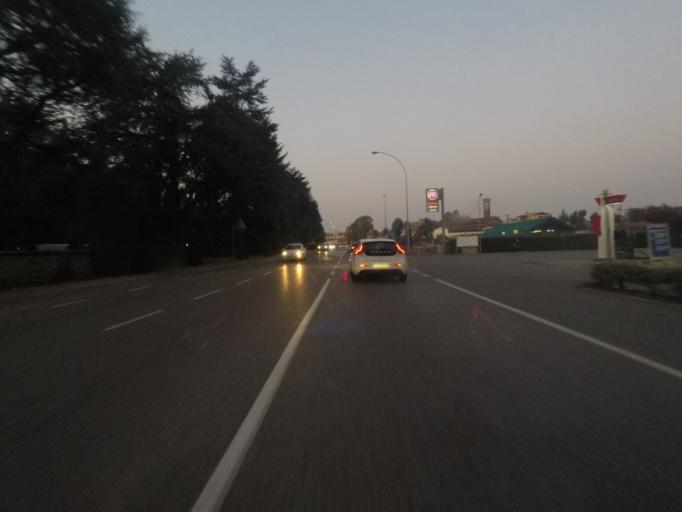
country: IT
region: Lombardy
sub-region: Provincia di Monza e Brianza
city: Concorezzo
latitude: 45.5878
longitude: 9.3306
